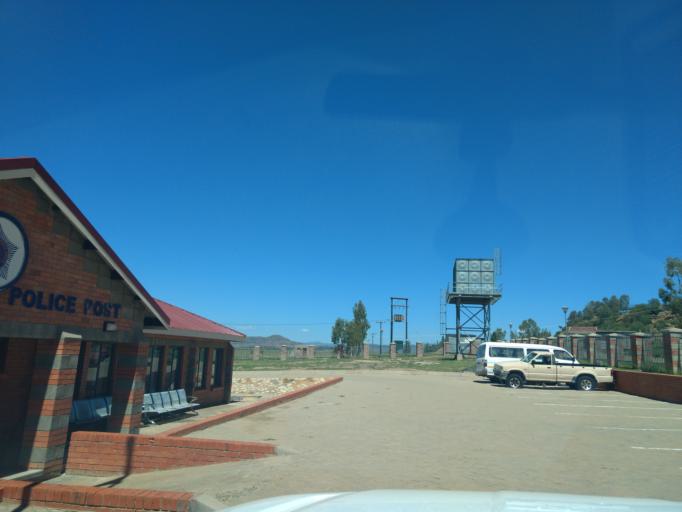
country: LS
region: Maseru
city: Maseru
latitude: -29.4956
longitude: 27.3755
